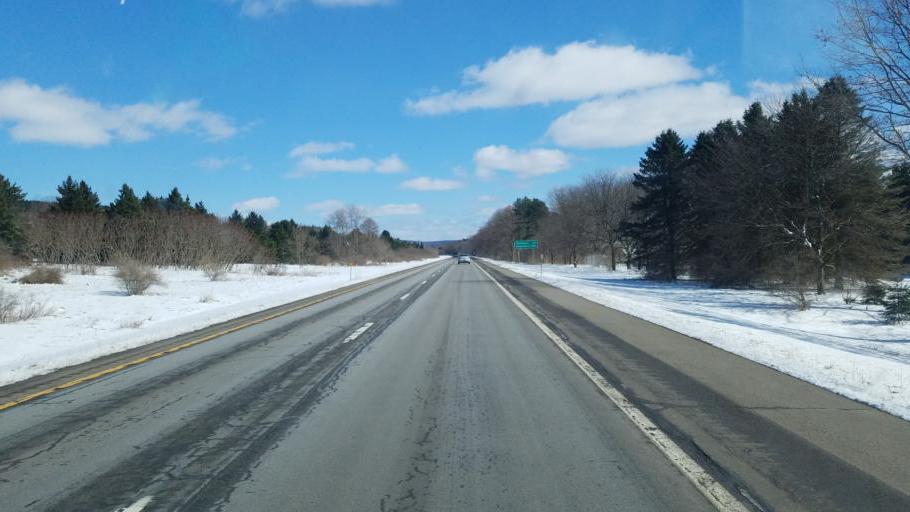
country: US
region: New York
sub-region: Chautauqua County
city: Falconer
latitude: 42.1363
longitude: -79.1560
